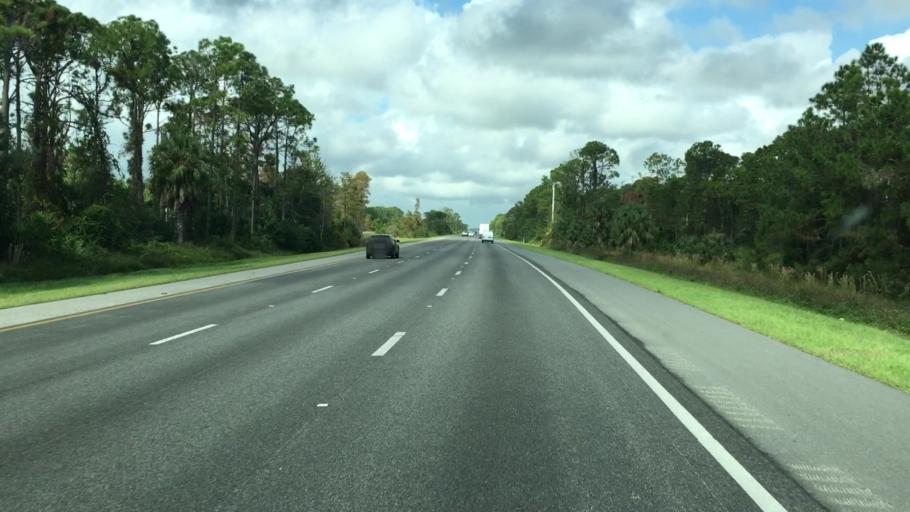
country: US
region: Florida
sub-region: Volusia County
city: Samsula-Spruce Creek
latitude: 29.0673
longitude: -81.0093
